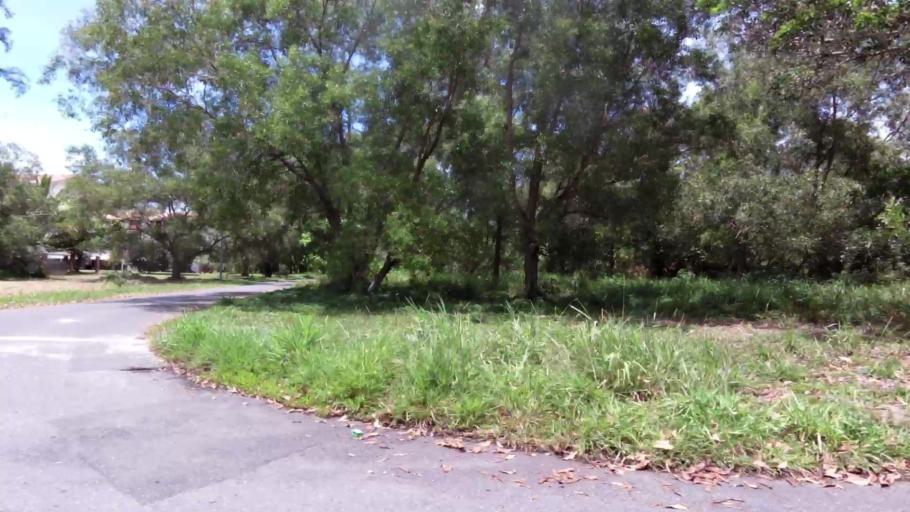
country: BN
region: Belait
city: Kuala Belait
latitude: 4.5917
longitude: 114.2522
